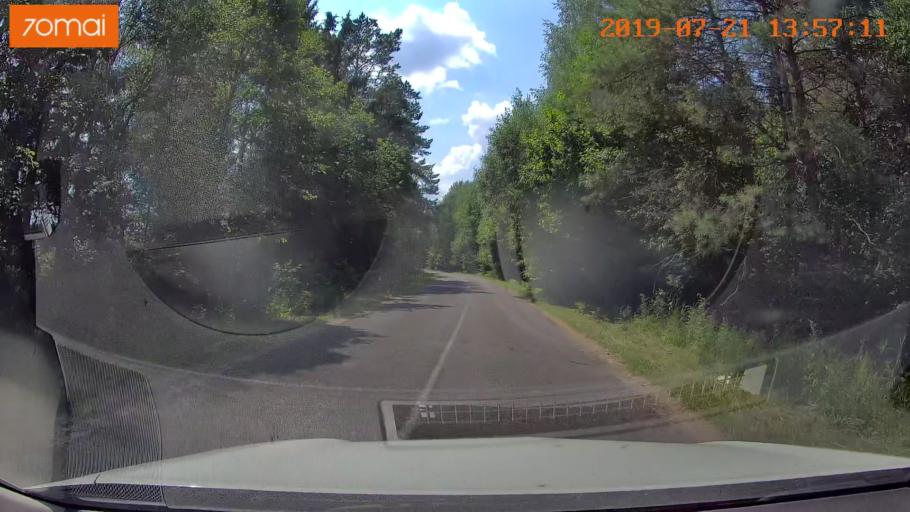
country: BY
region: Grodnenskaya
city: Lyubcha
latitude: 53.7750
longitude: 26.0906
